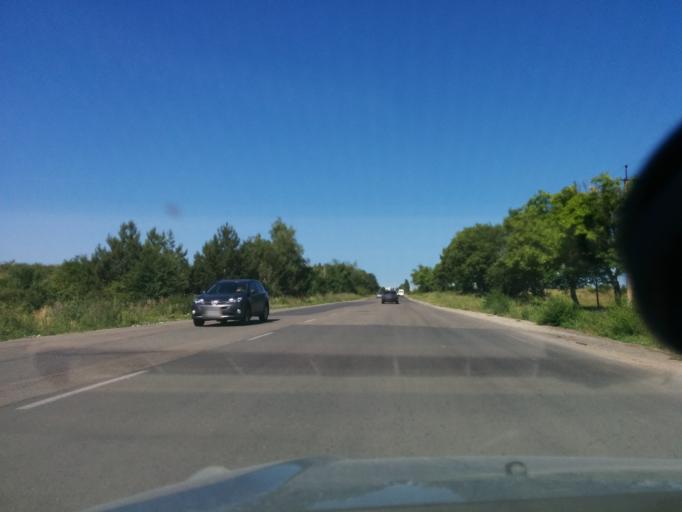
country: MD
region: Chisinau
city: Ciorescu
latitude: 47.0630
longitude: 28.9691
